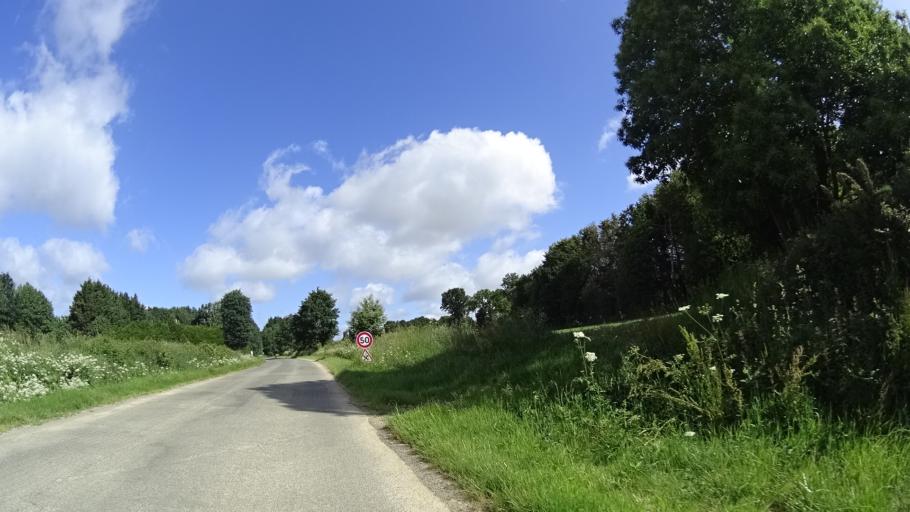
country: FR
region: Brittany
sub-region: Departement d'Ille-et-Vilaine
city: La Chapelle-des-Fougeretz
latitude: 48.1888
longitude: -1.7200
